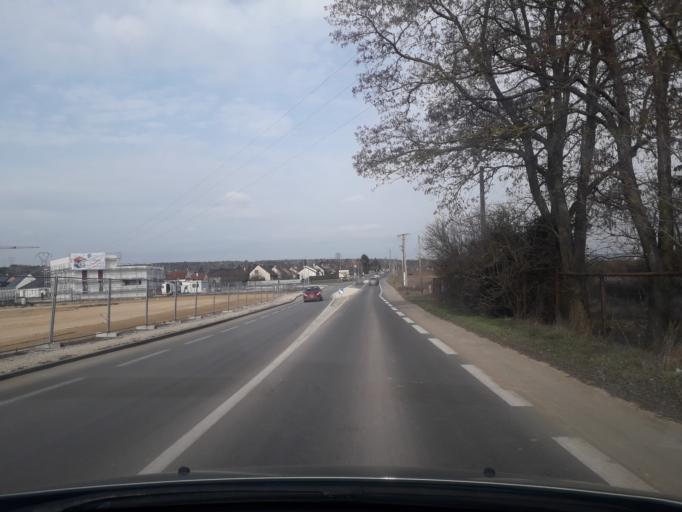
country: FR
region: Bourgogne
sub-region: Departement de la Cote-d'Or
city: Ahuy
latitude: 47.3618
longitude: 5.0308
